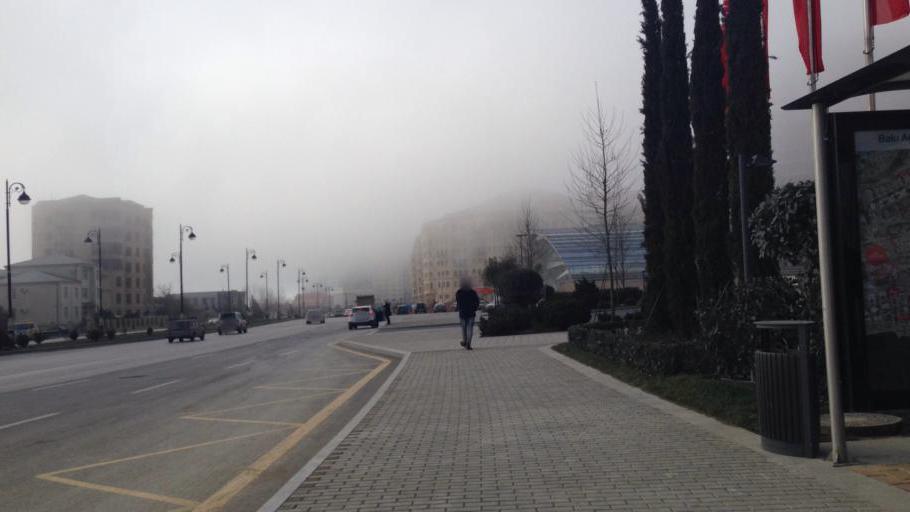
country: AZ
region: Baki
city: Baku
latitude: 40.3796
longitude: 49.8831
